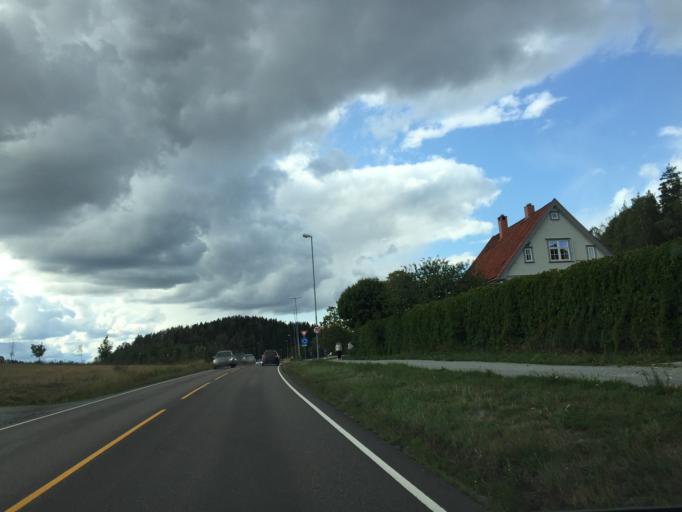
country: NO
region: Ostfold
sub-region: Askim
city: Askim
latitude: 59.5860
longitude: 11.1241
